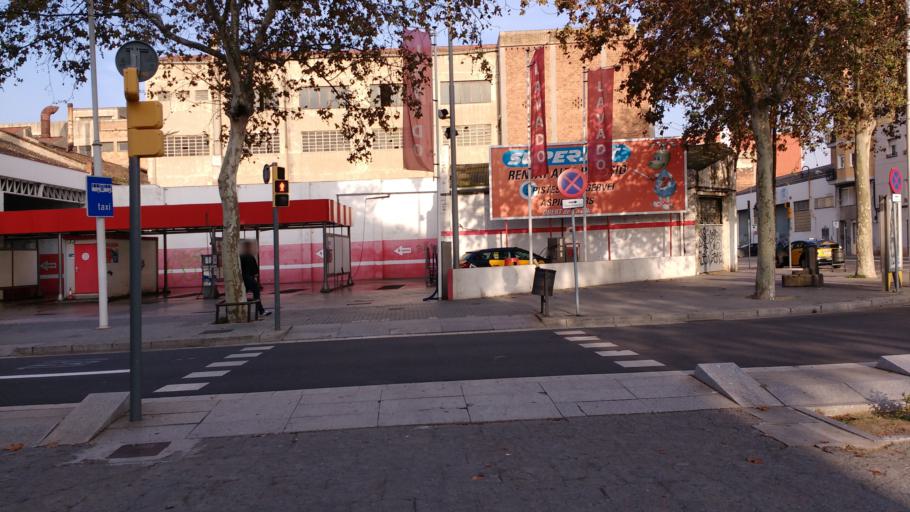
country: ES
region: Catalonia
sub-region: Provincia de Barcelona
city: Sant Marti
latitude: 41.3944
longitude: 2.2006
